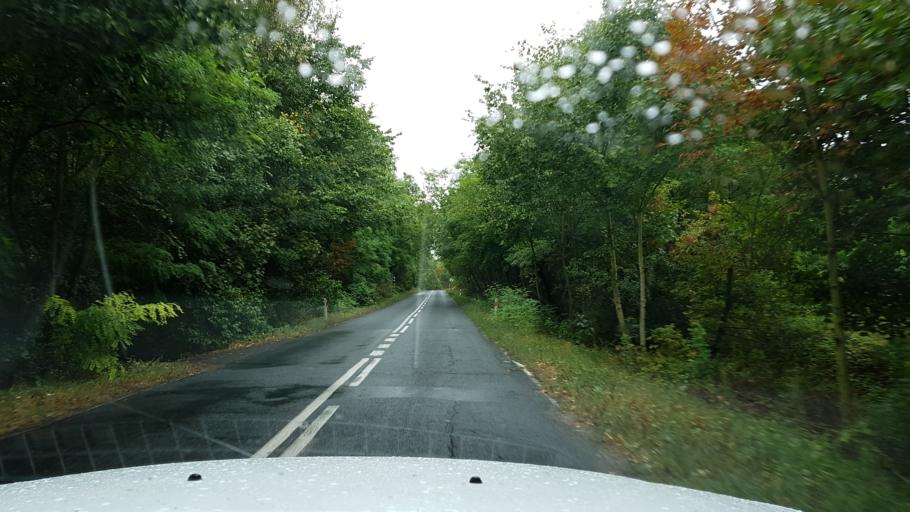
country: PL
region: West Pomeranian Voivodeship
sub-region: Powiat gryfinski
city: Cedynia
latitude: 52.8352
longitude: 14.1273
